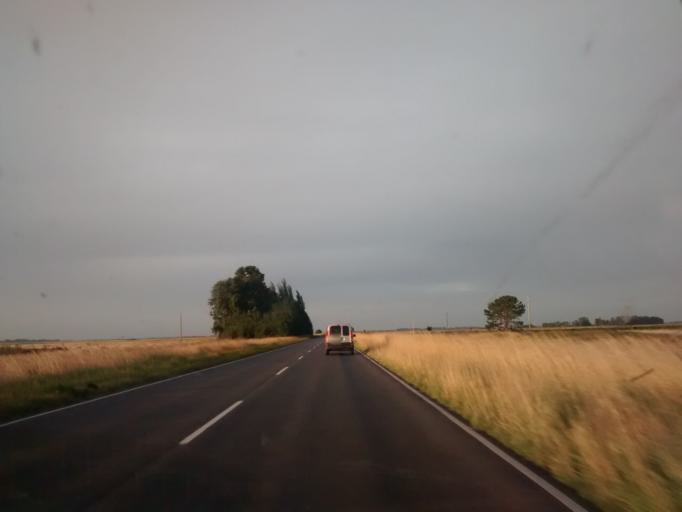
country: AR
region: Buenos Aires
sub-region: Partido de General Belgrano
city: General Belgrano
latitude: -35.9540
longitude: -58.6207
